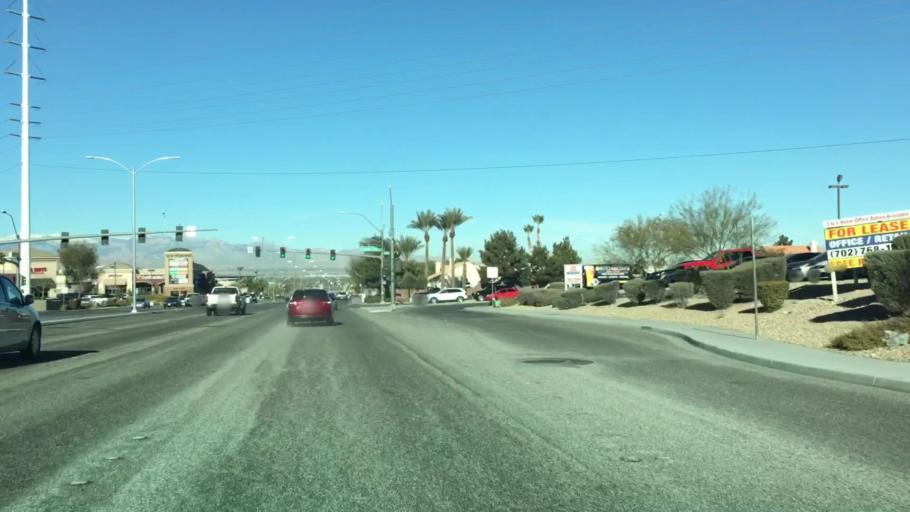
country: US
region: Nevada
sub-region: Clark County
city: Whitney
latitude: 36.0021
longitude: -115.1081
